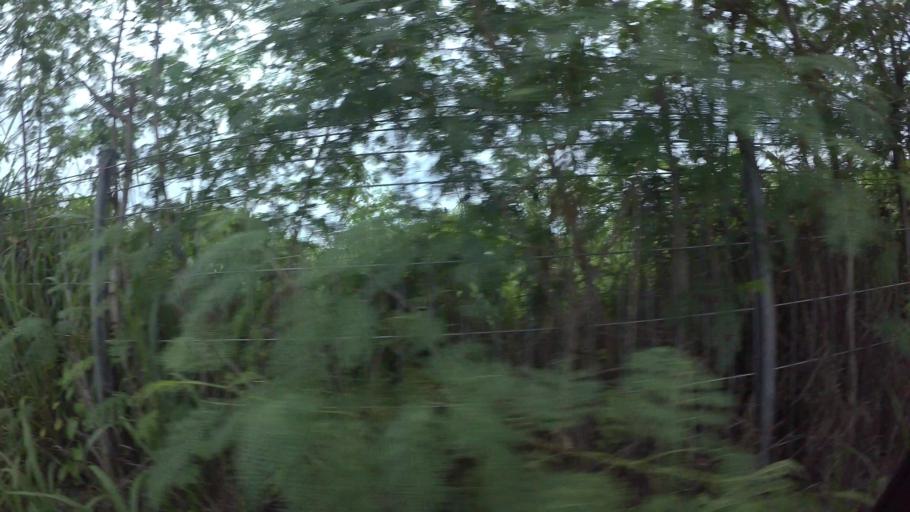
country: TH
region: Chon Buri
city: Si Racha
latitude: 13.1364
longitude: 100.9448
